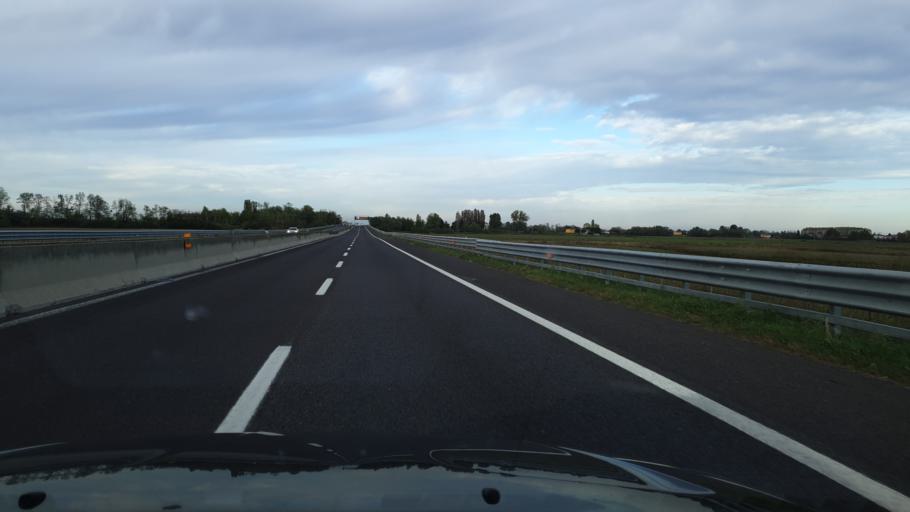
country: IT
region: Veneto
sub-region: Provincia di Rovigo
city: Grignano Polesine
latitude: 45.0657
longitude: 11.7290
